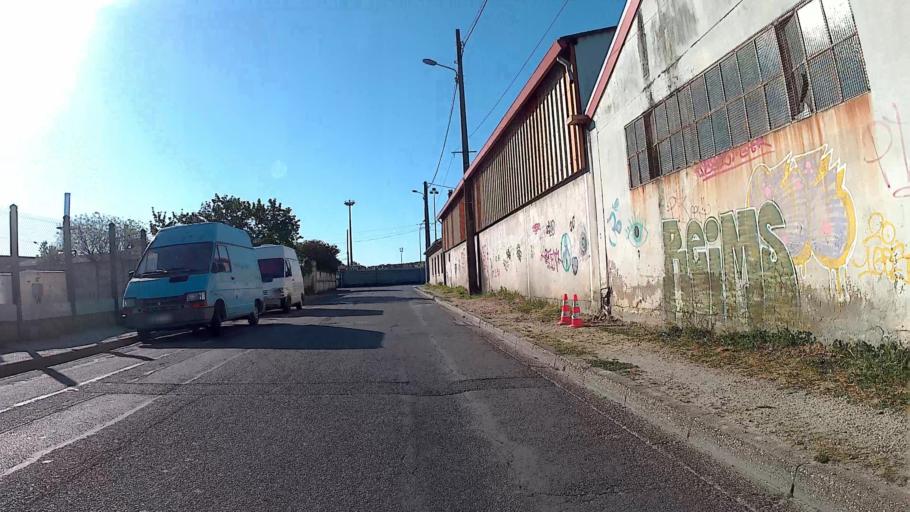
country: FR
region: Aquitaine
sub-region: Departement de la Gironde
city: Begles
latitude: 44.8157
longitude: -0.5406
